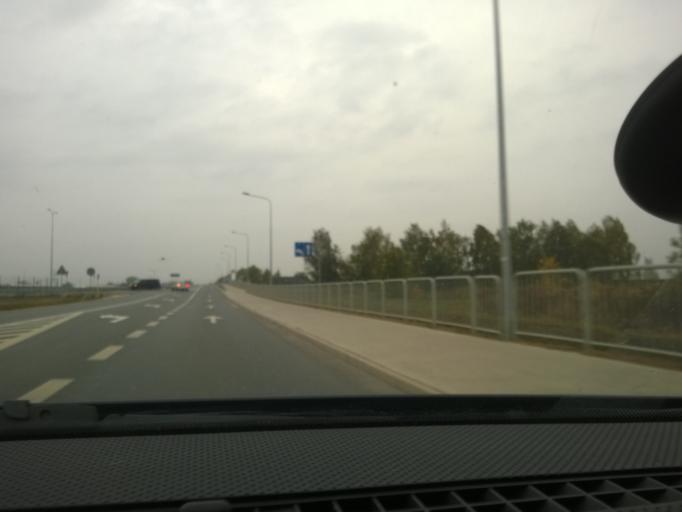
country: PL
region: Masovian Voivodeship
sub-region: Powiat pruszkowski
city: Nowe Grocholice
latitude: 52.1433
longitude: 20.8881
